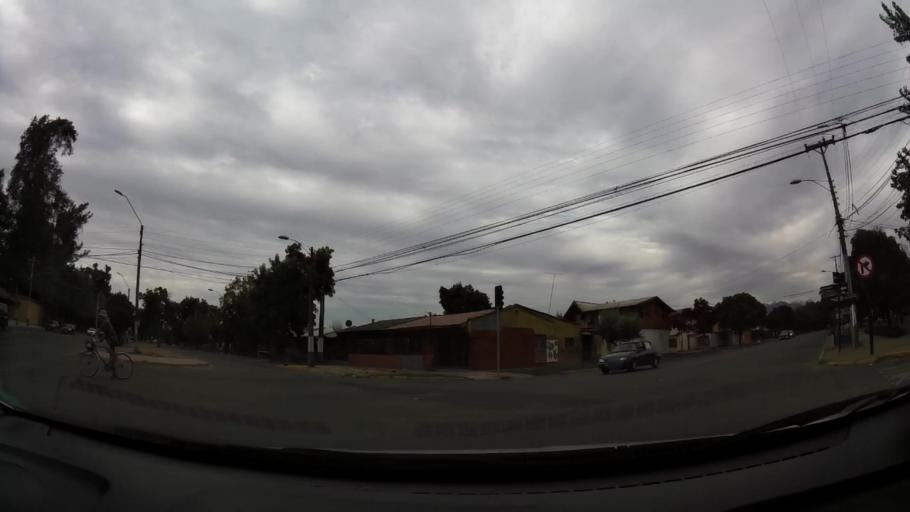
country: CL
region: O'Higgins
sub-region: Provincia de Cachapoal
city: Rancagua
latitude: -34.1589
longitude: -70.7440
